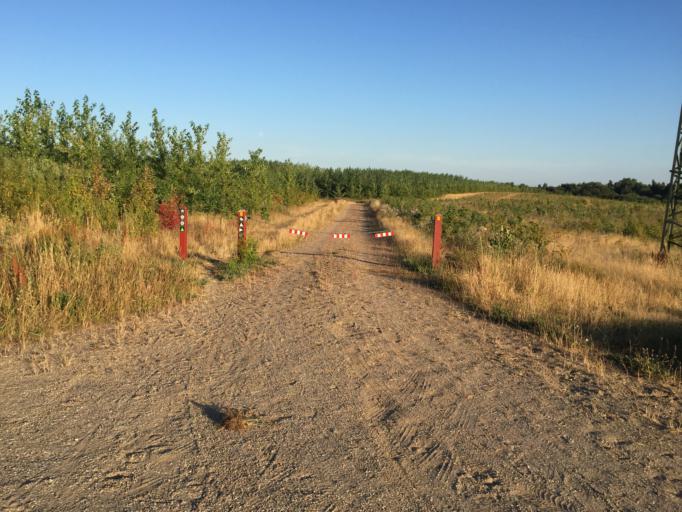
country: DK
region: South Denmark
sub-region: Odense Kommune
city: Bellinge
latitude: 55.3798
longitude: 10.2943
